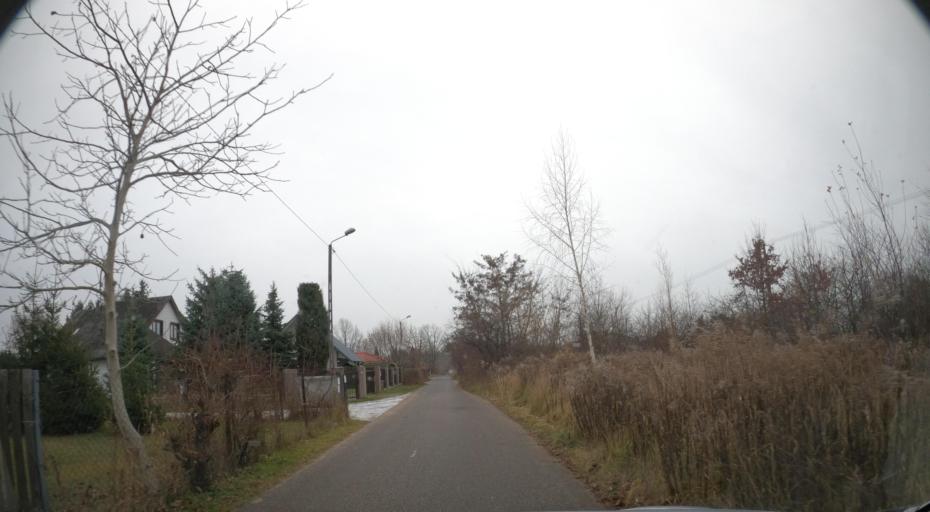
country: PL
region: Masovian Voivodeship
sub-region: Powiat radomski
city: Jastrzebia
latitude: 51.4307
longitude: 21.2304
